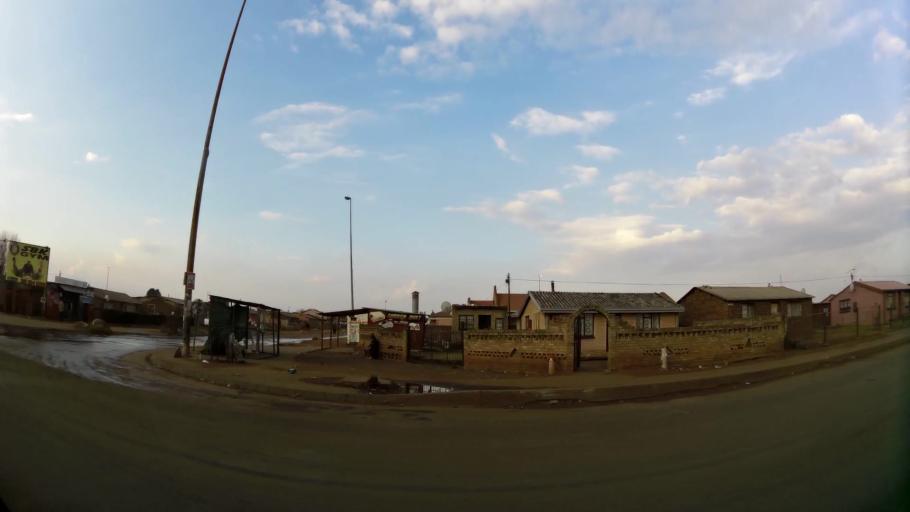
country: ZA
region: Gauteng
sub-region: City of Johannesburg Metropolitan Municipality
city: Orange Farm
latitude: -26.5760
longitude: 27.8402
